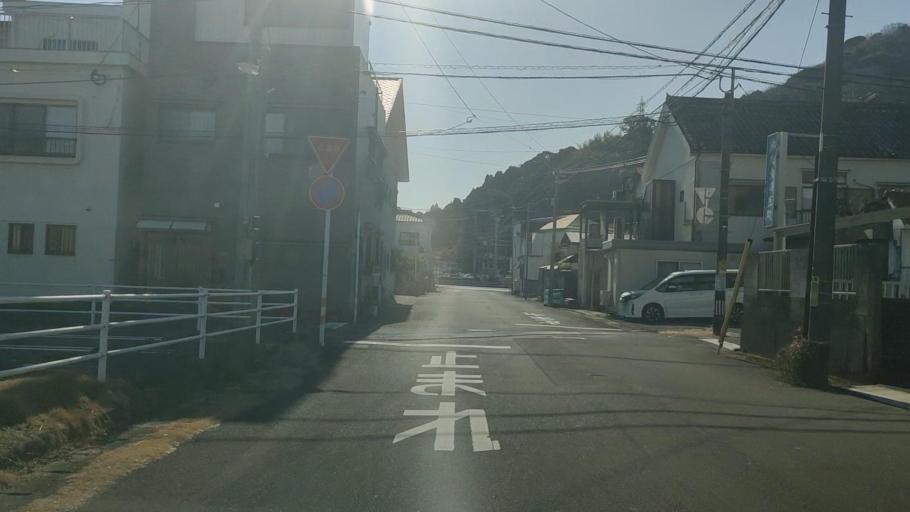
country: JP
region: Oita
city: Saiki
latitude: 32.9717
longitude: 131.9033
